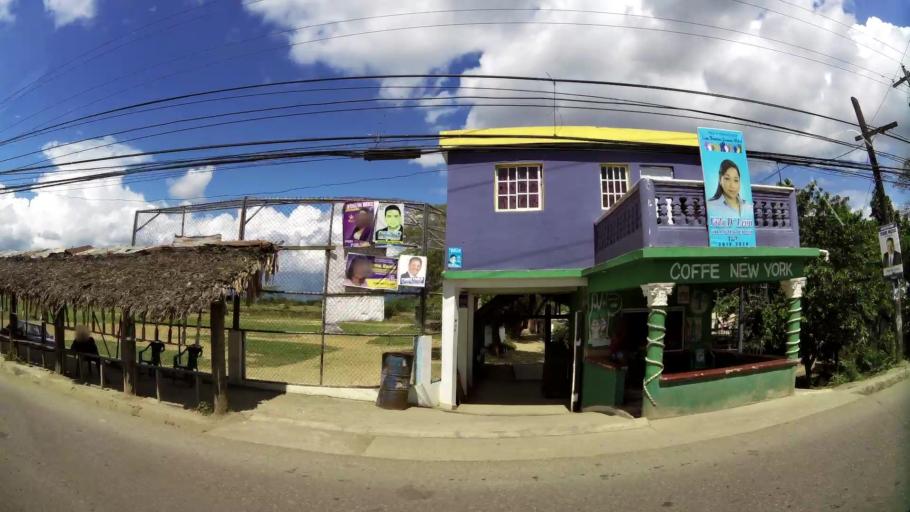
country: DO
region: Santiago
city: Santiago de los Caballeros
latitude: 19.4113
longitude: -70.6736
